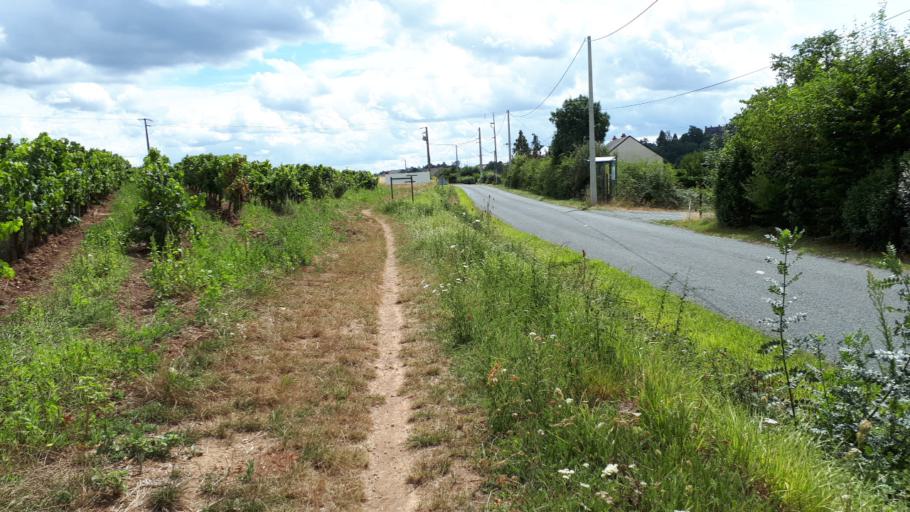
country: FR
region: Pays de la Loire
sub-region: Departement de Maine-et-Loire
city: Rochefort-sur-Loire
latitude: 47.3286
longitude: -0.6868
